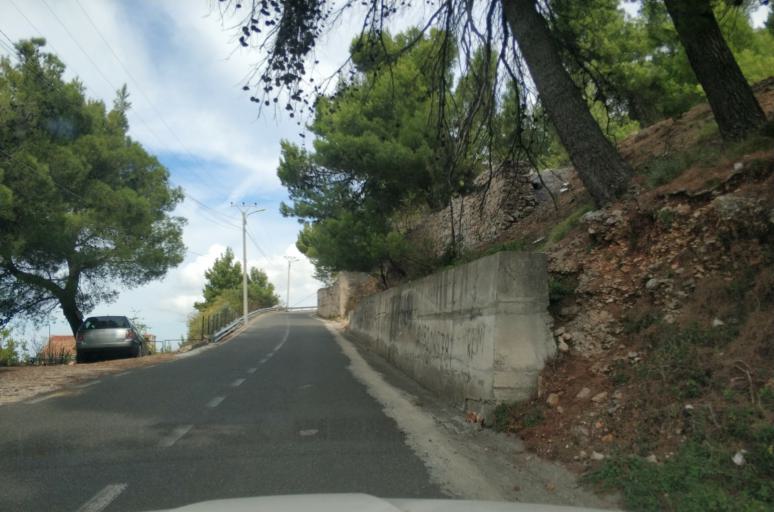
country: AL
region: Durres
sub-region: Rrethi i Krujes
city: Kruje
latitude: 41.5154
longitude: 19.7939
